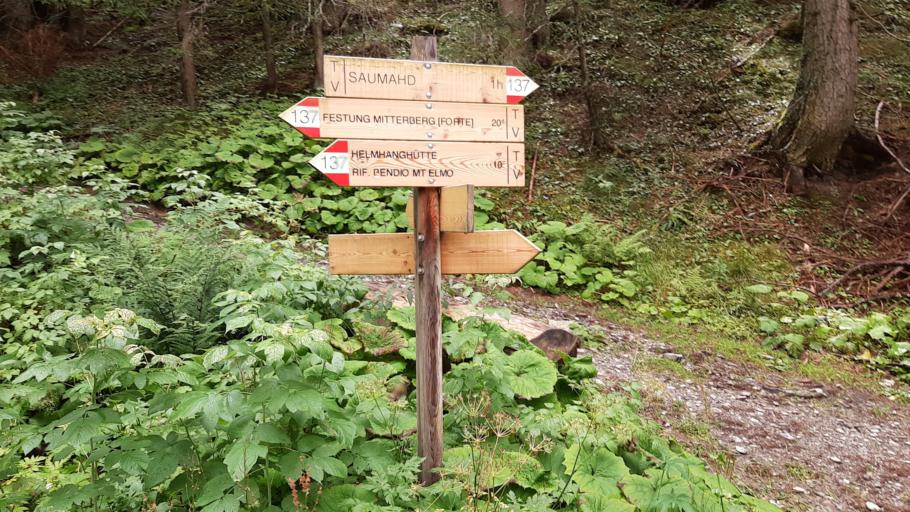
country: IT
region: Trentino-Alto Adige
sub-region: Bolzano
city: Sesto
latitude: 46.6982
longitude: 12.3795
